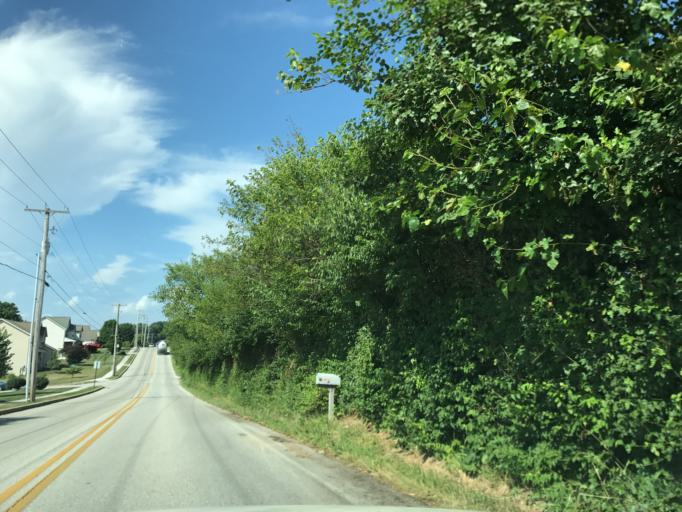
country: US
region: Pennsylvania
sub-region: York County
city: Pennville
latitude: 39.7658
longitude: -76.9855
